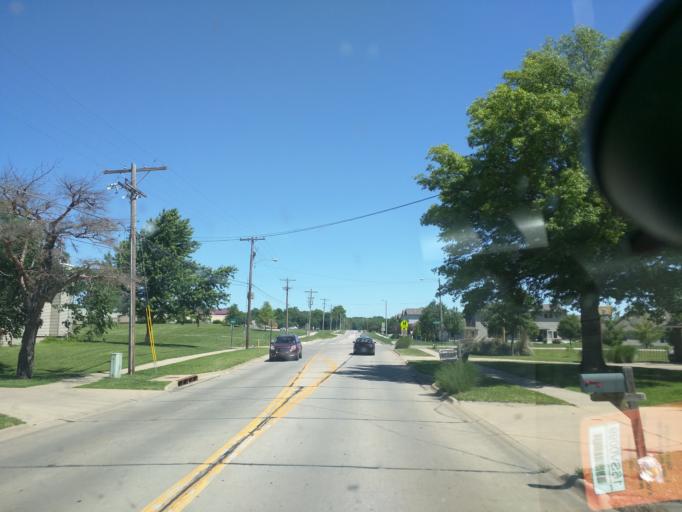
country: US
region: Kansas
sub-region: Riley County
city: Manhattan
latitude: 39.2101
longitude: -96.6075
